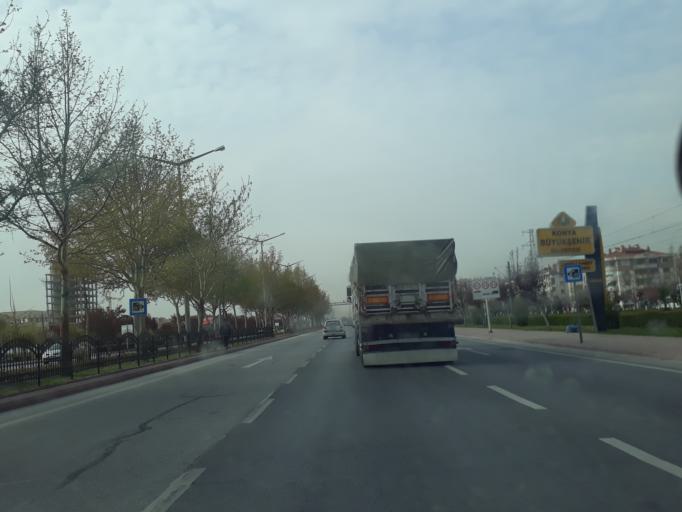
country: TR
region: Konya
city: Selcuklu
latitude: 37.9648
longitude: 32.5148
